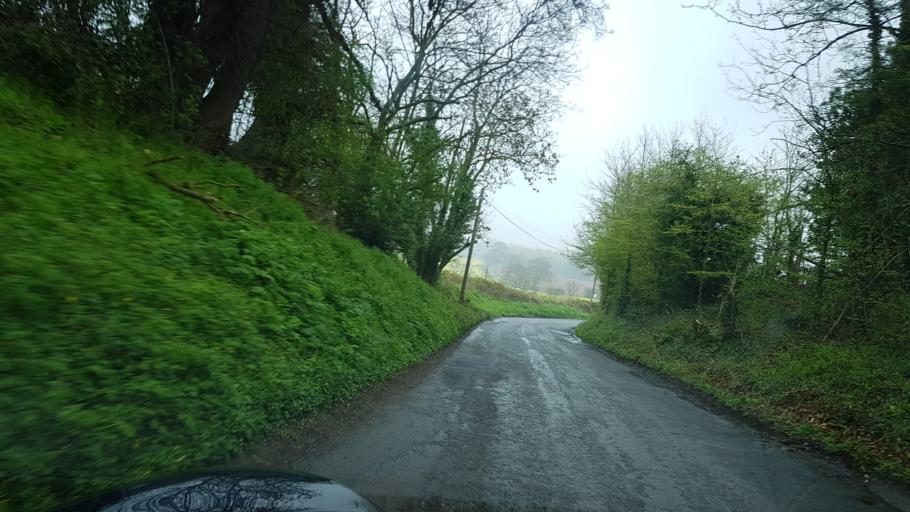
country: GB
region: England
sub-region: Herefordshire
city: Yatton
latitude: 52.0017
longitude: -2.5181
